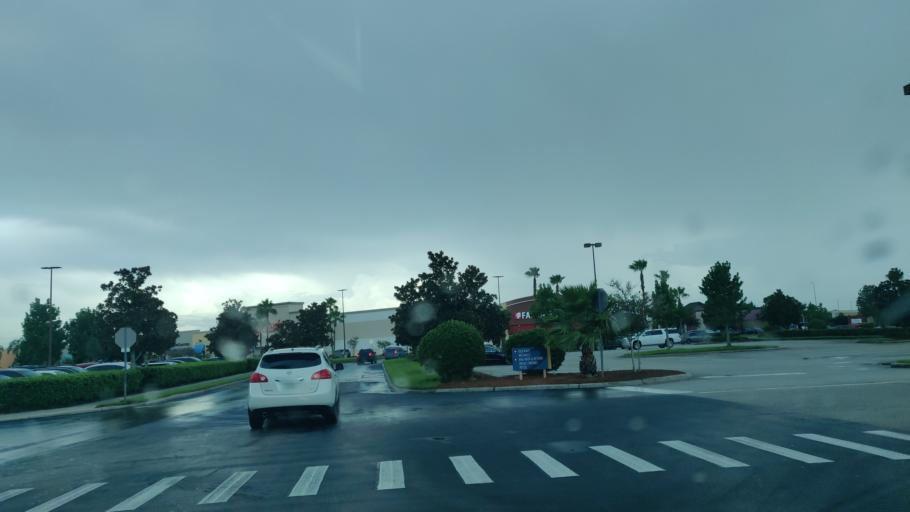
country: US
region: Florida
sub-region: Orange County
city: Hunters Creek
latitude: 28.3442
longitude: -81.4235
